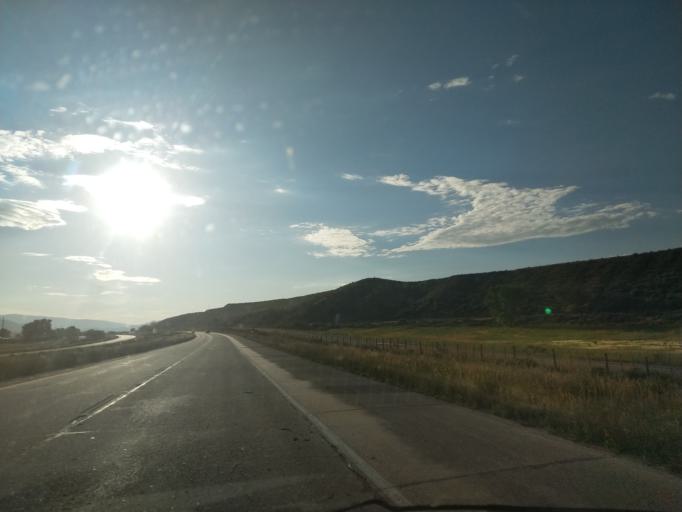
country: US
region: Colorado
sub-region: Garfield County
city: Rifle
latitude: 39.5298
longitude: -107.7311
